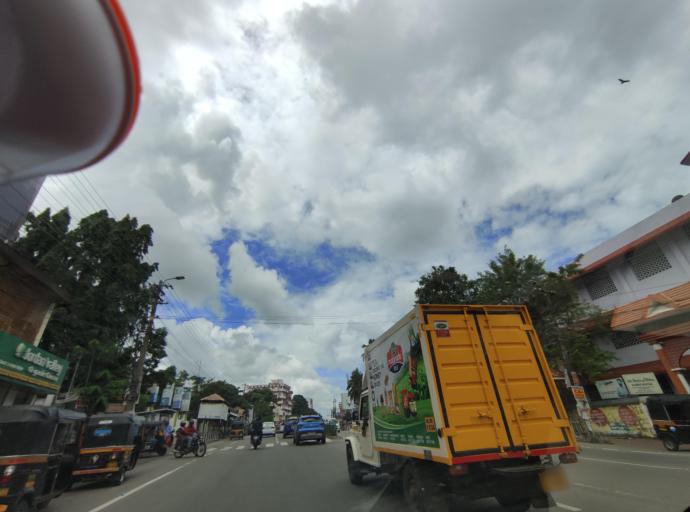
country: IN
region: Kerala
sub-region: Thiruvananthapuram
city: Thiruvananthapuram
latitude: 8.5234
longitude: 76.9405
